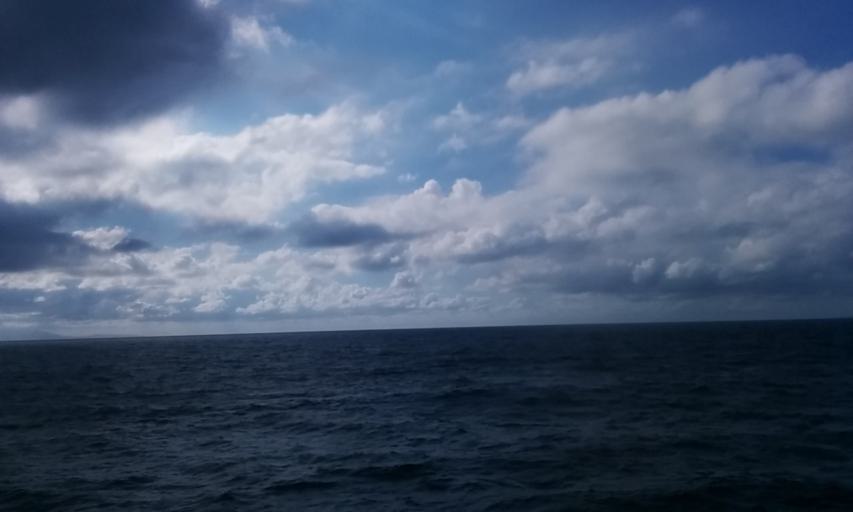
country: JP
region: Kagoshima
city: Nishinoomote
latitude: 30.5969
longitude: 130.5955
